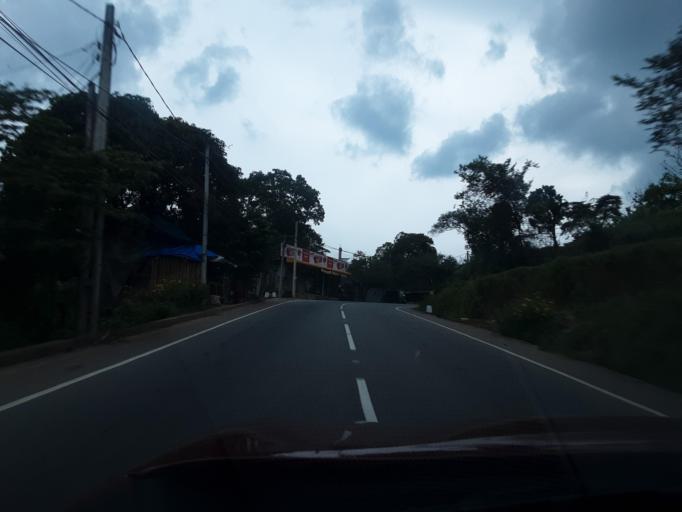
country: LK
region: Central
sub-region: Nuwara Eliya District
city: Nuwara Eliya
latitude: 6.9012
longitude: 80.9027
